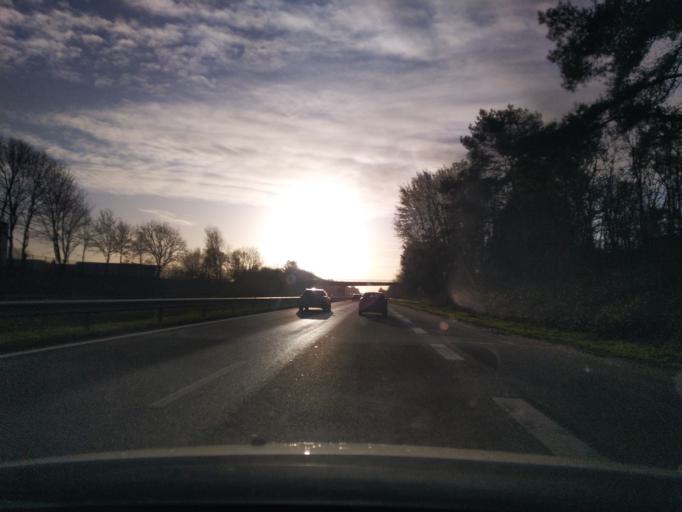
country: FR
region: Haute-Normandie
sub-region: Departement de la Seine-Maritime
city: Maromme
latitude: 49.4796
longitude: 1.0131
